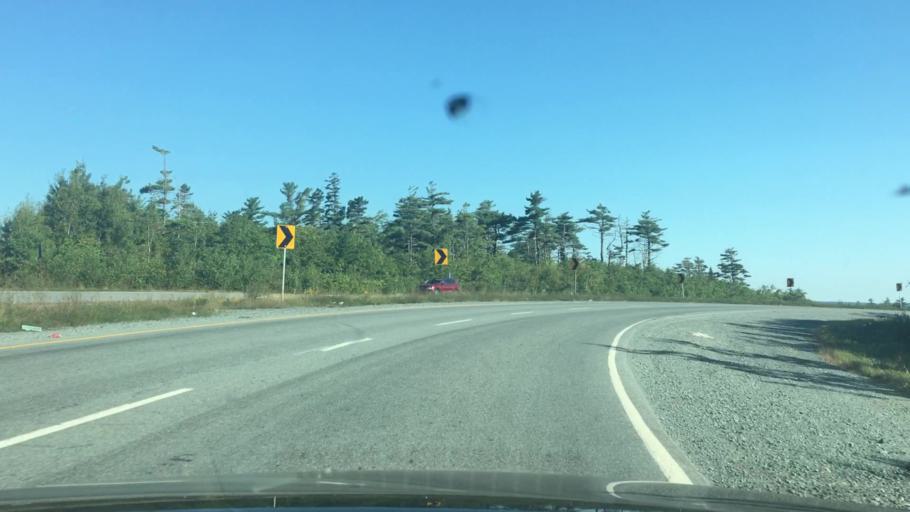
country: CA
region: Nova Scotia
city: Dartmouth
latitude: 44.7211
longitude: -63.5809
